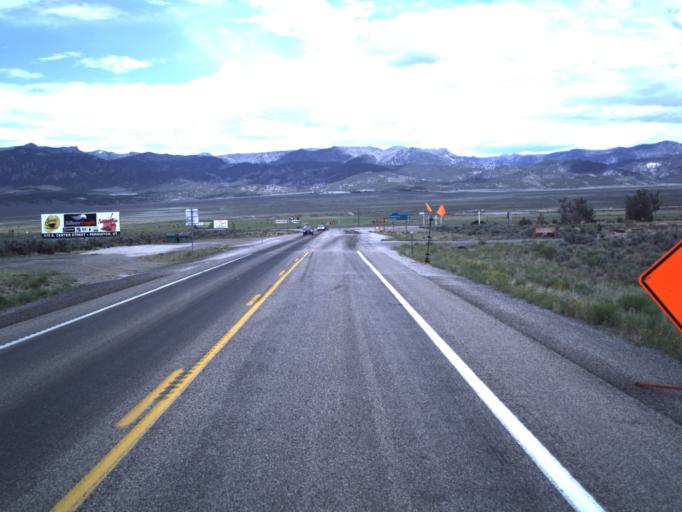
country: US
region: Utah
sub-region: Garfield County
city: Panguitch
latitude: 37.9655
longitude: -112.4161
